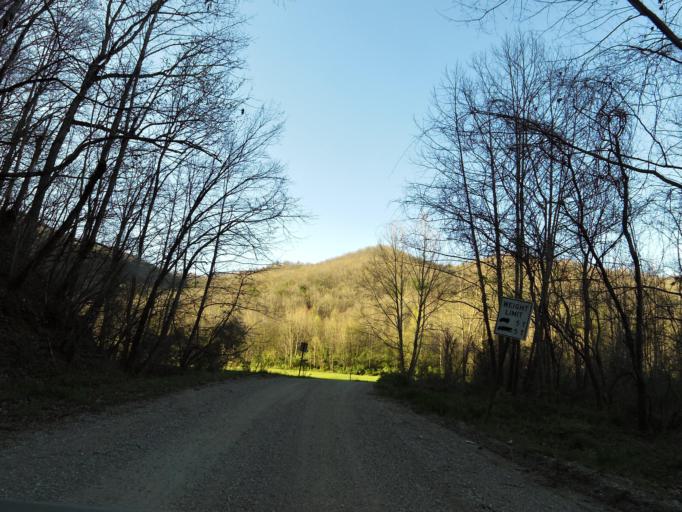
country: US
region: Tennessee
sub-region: Scott County
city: Huntsville
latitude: 36.2691
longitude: -84.3926
